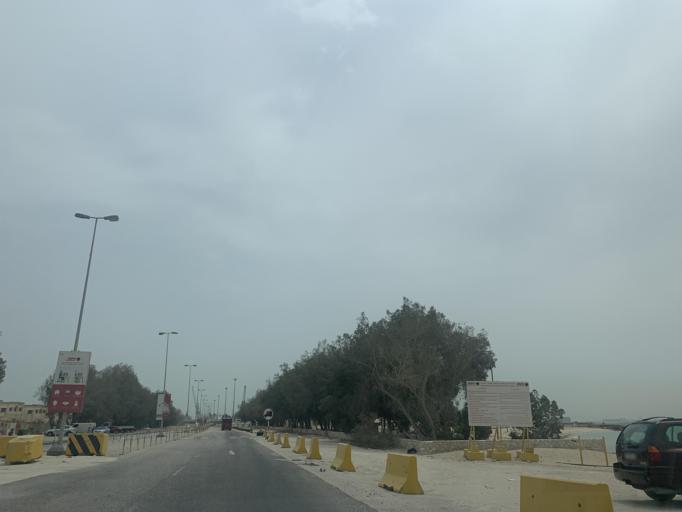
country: BH
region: Muharraq
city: Al Hadd
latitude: 26.1983
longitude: 50.6623
